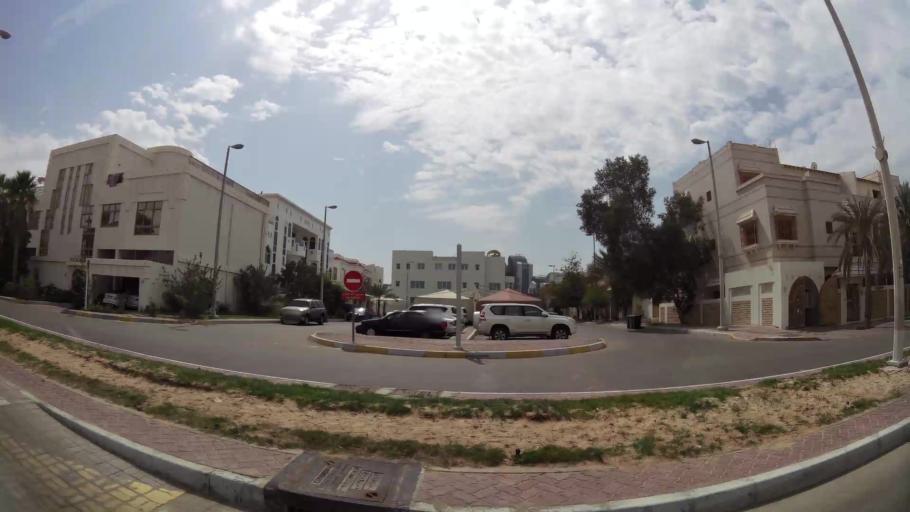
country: AE
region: Abu Dhabi
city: Abu Dhabi
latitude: 24.4605
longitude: 54.3438
